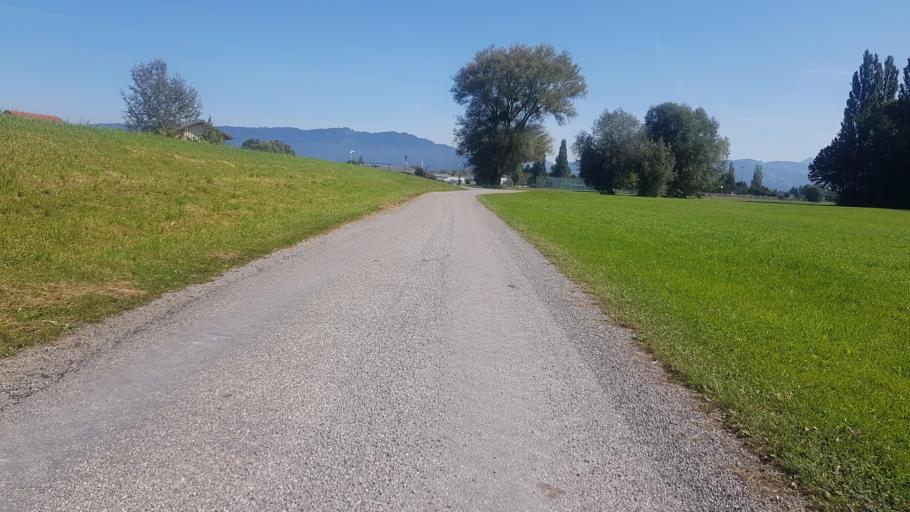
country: AT
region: Vorarlberg
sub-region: Politischer Bezirk Bregenz
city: Fussach
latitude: 47.4863
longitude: 9.6539
